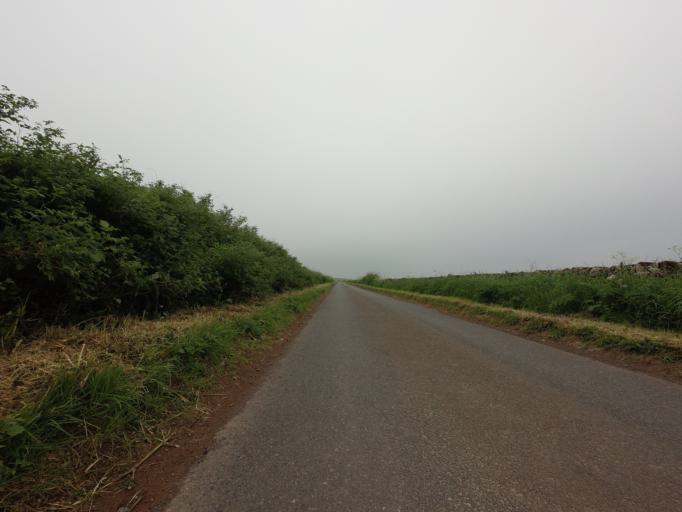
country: GB
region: Scotland
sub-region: Perth and Kinross
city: Abernethy
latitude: 56.2663
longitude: -3.3001
